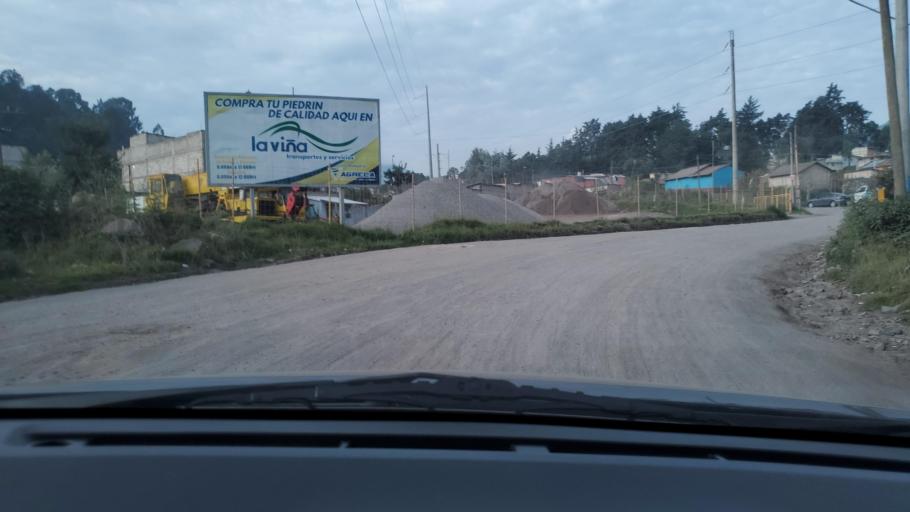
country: GT
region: Quetzaltenango
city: Quetzaltenango
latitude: 14.8257
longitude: -91.5359
